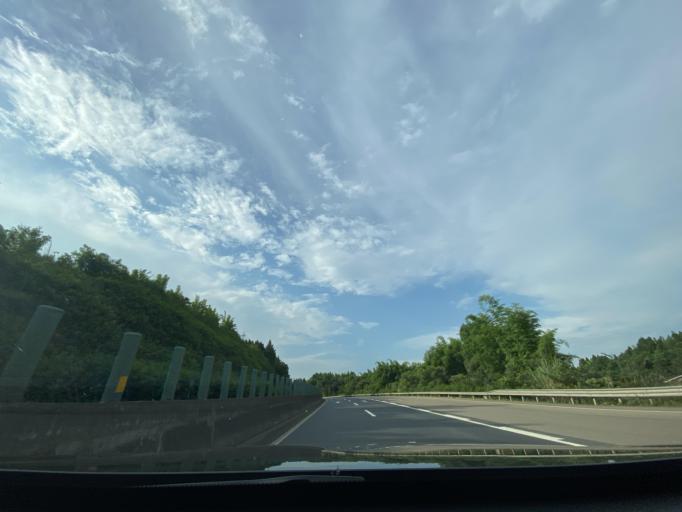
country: CN
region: Sichuan
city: Yanjiang
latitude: 30.0884
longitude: 104.5994
